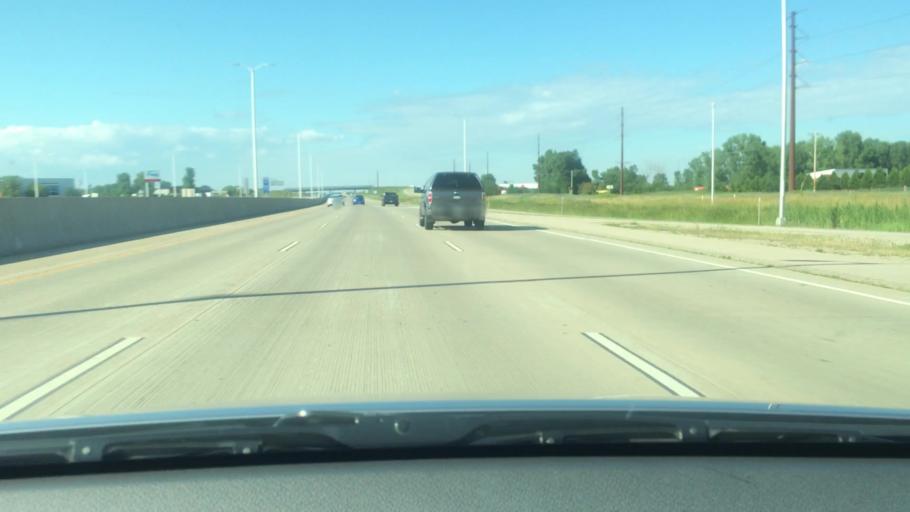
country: US
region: Wisconsin
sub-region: Winnebago County
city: Oshkosh
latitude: 44.0614
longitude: -88.5727
